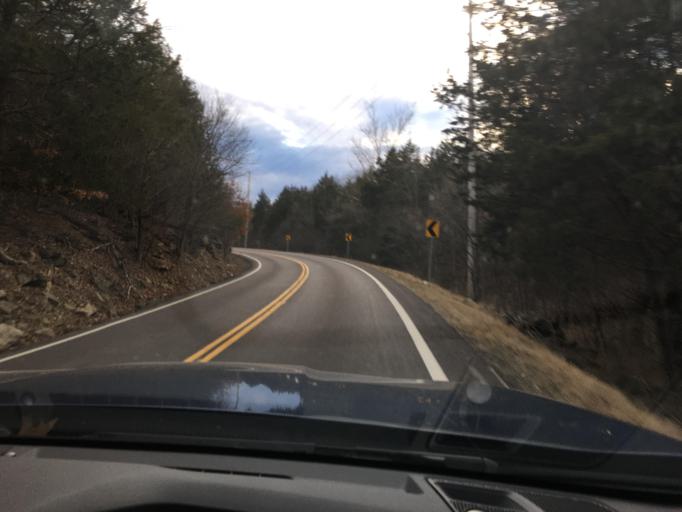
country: US
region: Missouri
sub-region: Jefferson County
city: De Soto
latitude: 38.1040
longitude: -90.5606
